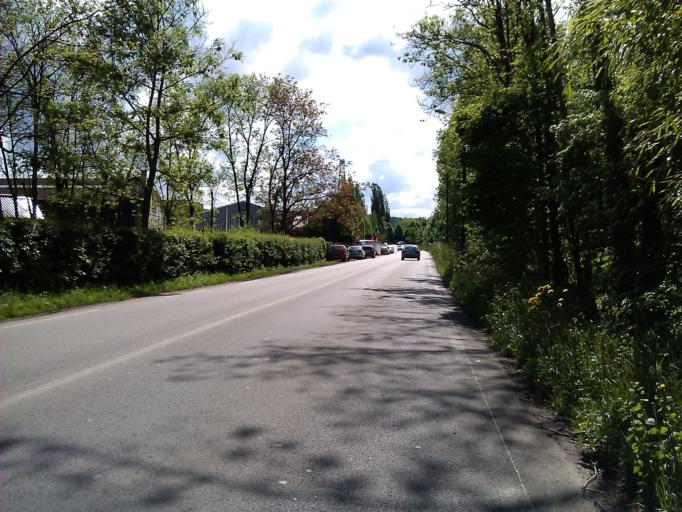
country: FR
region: Franche-Comte
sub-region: Departement du Doubs
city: Colombier-Fontaine
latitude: 47.4553
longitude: 6.6859
